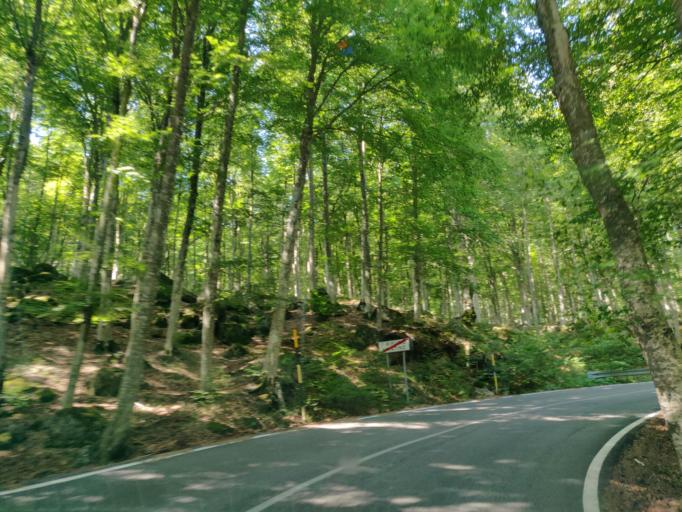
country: IT
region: Tuscany
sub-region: Provincia di Siena
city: Abbadia San Salvatore
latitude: 42.9022
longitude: 11.6292
